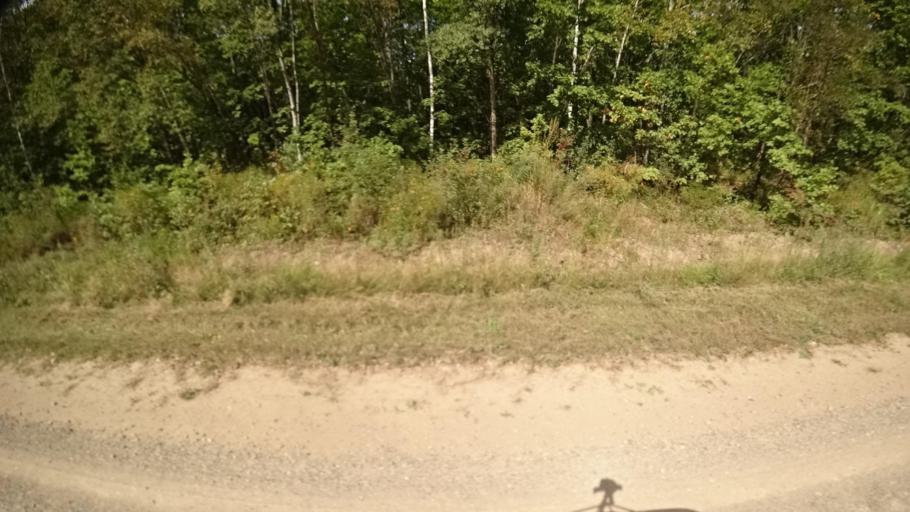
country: RU
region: Primorskiy
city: Yakovlevka
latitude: 44.6632
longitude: 133.6035
